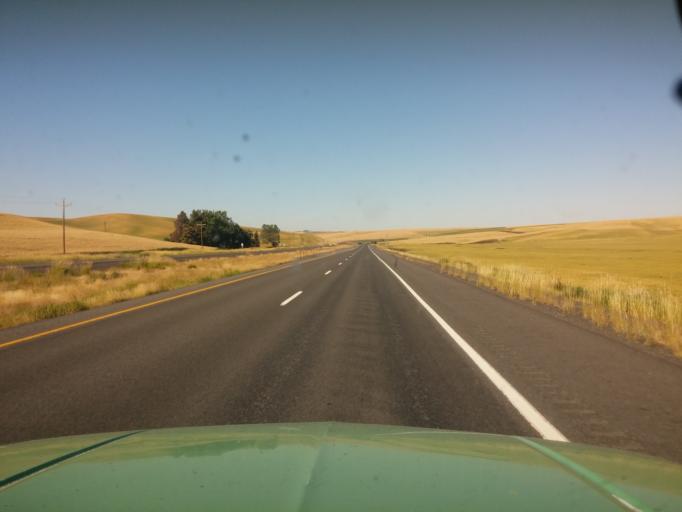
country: US
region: Idaho
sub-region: Nez Perce County
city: Lewiston
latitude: 46.4946
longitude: -117.0074
